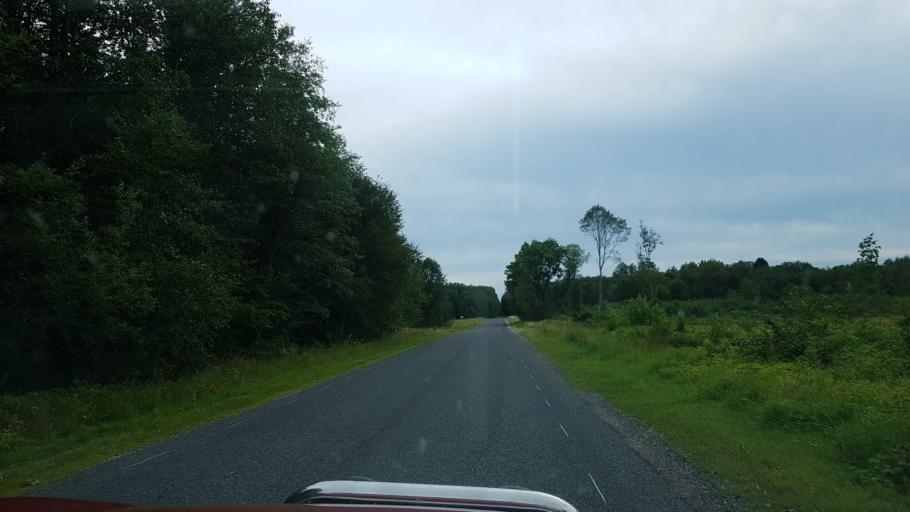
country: EE
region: Laeaene
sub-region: Lihula vald
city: Lihula
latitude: 58.8633
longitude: 23.8284
